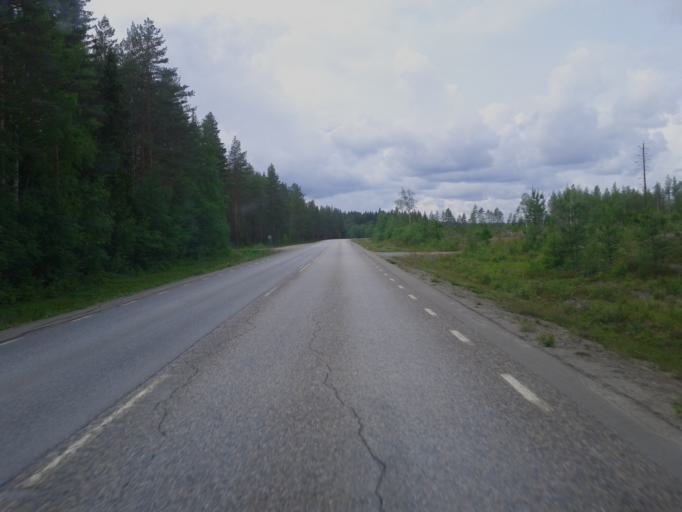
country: SE
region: Vaesterbotten
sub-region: Norsjo Kommun
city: Norsjoe
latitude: 64.9803
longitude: 19.5814
